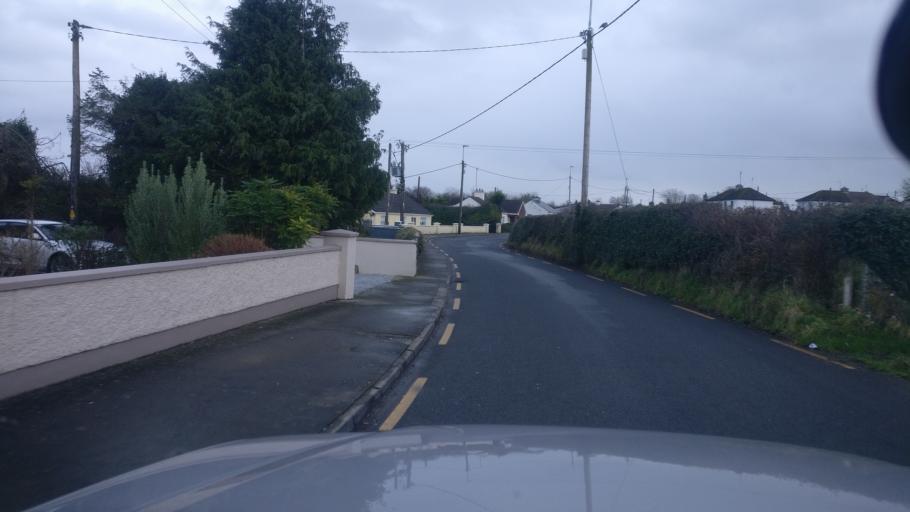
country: IE
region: Munster
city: Nenagh Bridge
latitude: 52.9933
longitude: -8.1244
